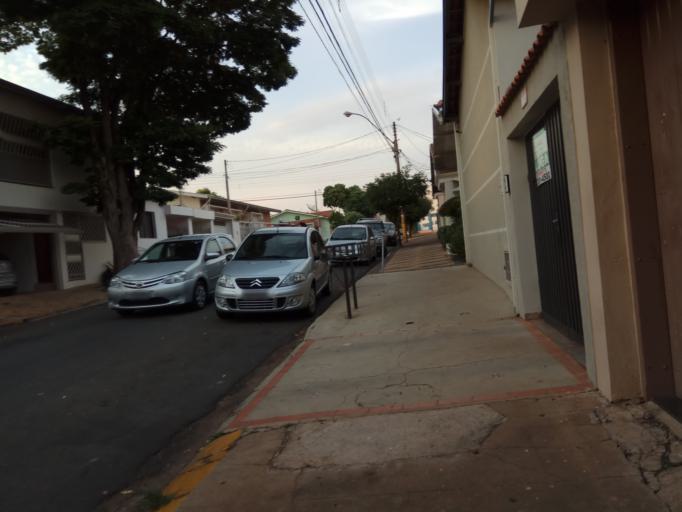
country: BR
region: Sao Paulo
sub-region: Piracicaba
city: Piracicaba
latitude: -22.7109
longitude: -47.6423
